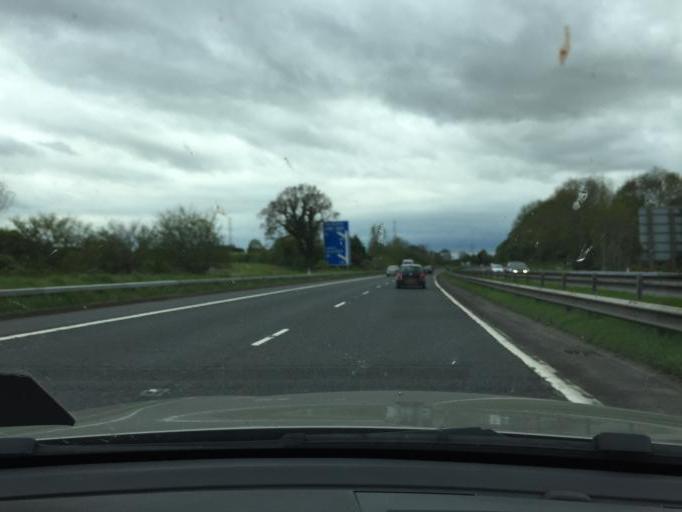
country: GB
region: Northern Ireland
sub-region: Lisburn District
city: Lisburn
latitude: 54.4979
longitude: -6.0417
